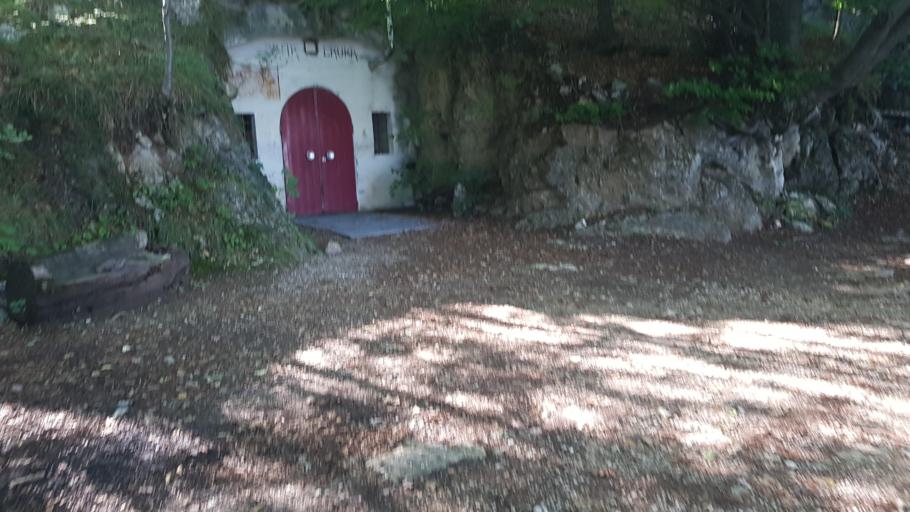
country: IT
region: Trentino-Alto Adige
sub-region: Provincia di Trento
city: Cadine
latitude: 46.0982
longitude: 11.0852
